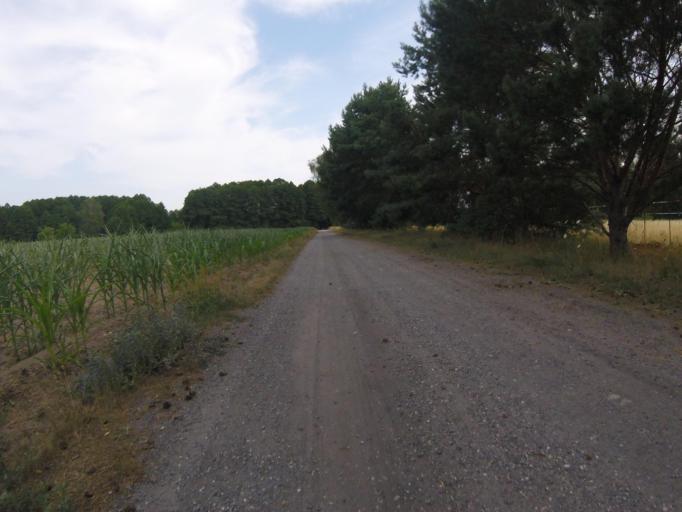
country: DE
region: Brandenburg
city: Erkner
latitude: 52.3109
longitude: 13.7545
